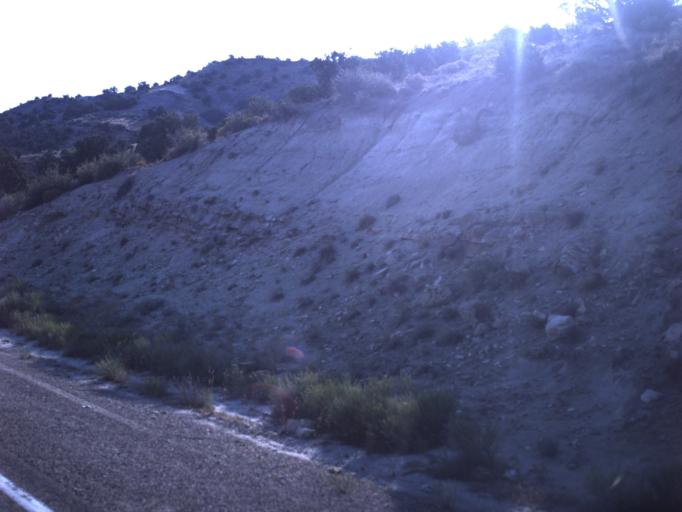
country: US
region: Utah
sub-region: Uintah County
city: Vernal
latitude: 40.5152
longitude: -109.5257
